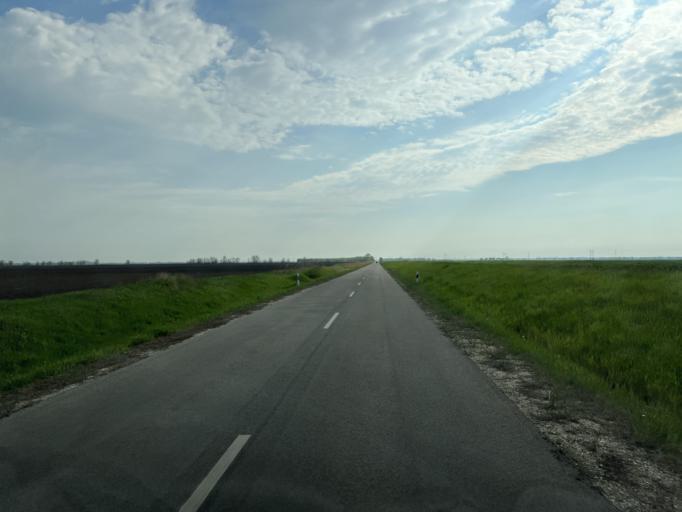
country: HU
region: Pest
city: Jaszkarajeno
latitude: 47.1088
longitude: 20.0477
